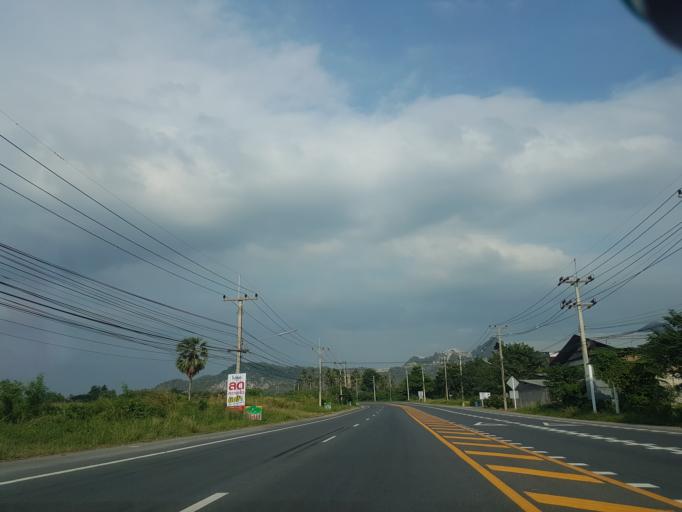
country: TH
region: Sara Buri
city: Phra Phutthabat
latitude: 14.6688
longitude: 100.7715
